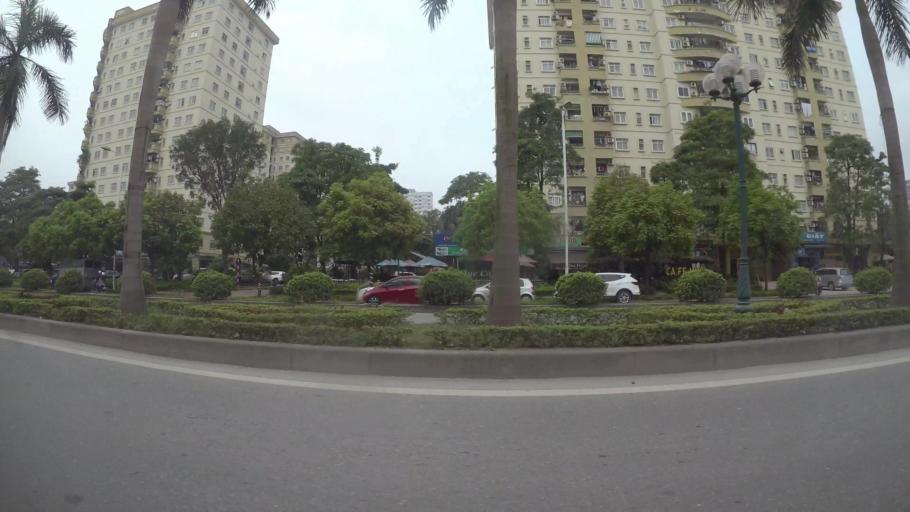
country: VN
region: Ha Noi
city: Cau Dien
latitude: 21.0288
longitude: 105.7651
